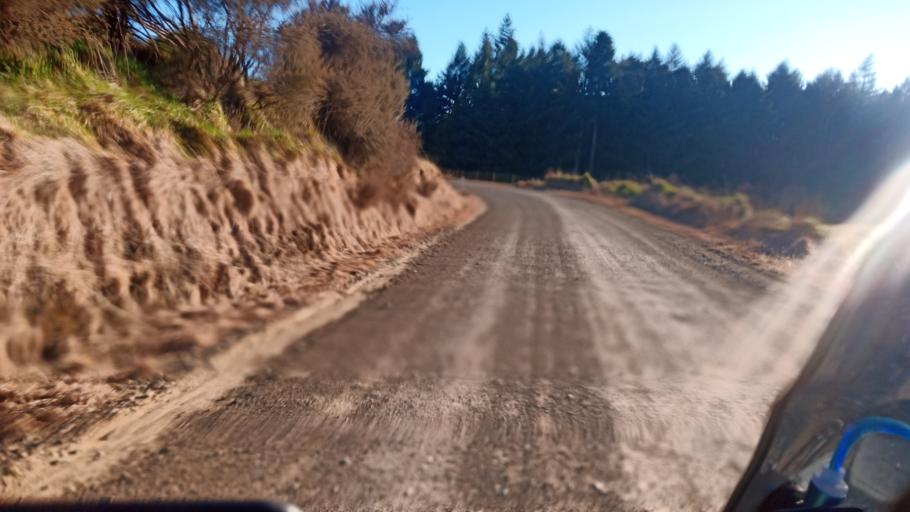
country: NZ
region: Bay of Plenty
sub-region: Opotiki District
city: Opotiki
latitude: -38.4595
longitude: 177.4265
